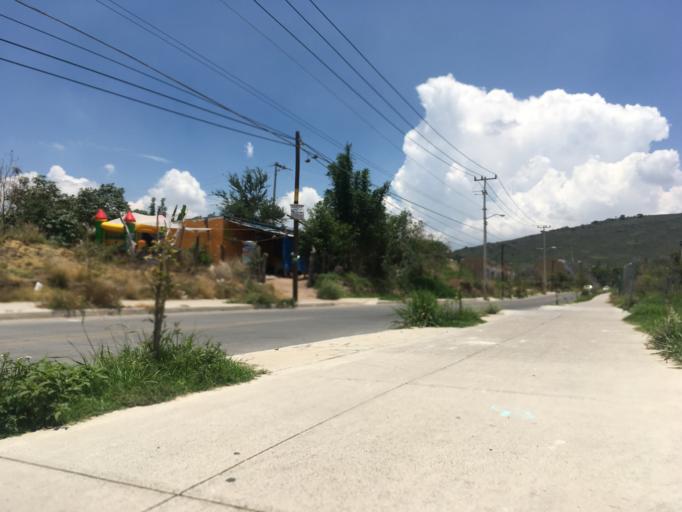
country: MX
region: Jalisco
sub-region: Tlajomulco de Zuniga
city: Jardines de San Sebastian
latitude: 20.5175
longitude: -103.4255
